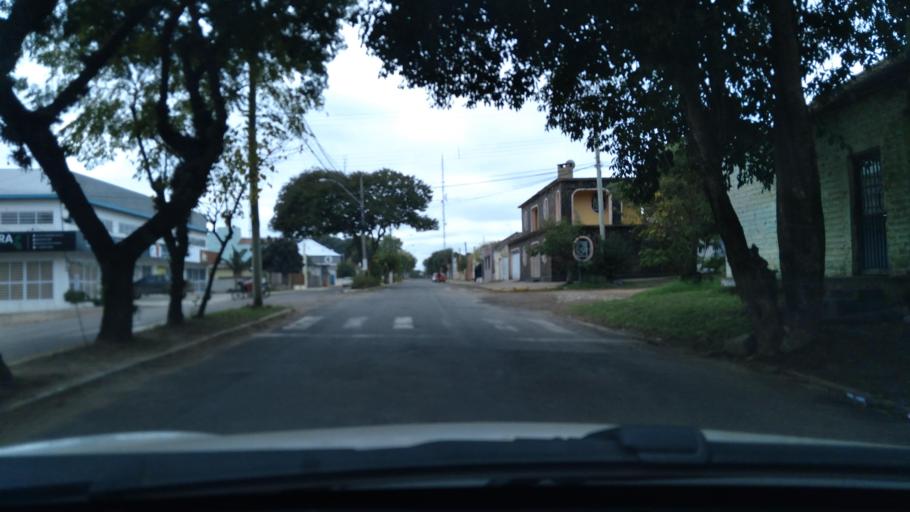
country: BR
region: Rio Grande do Sul
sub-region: Dom Pedrito
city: Dom Pedrito
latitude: -30.9701
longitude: -54.6730
